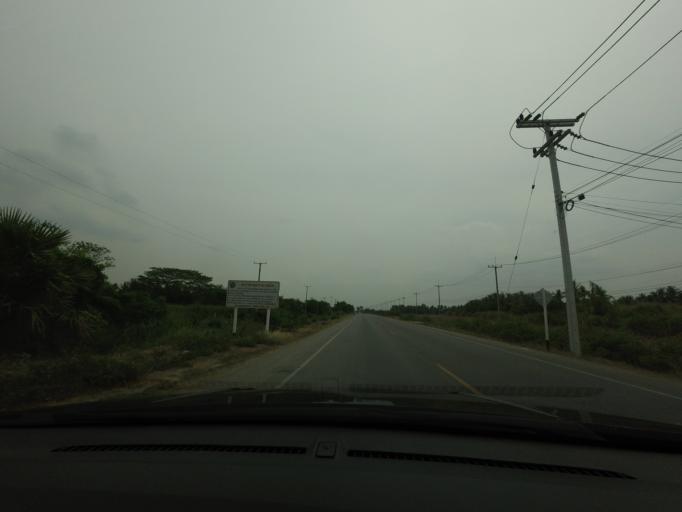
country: TH
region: Phetchaburi
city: Ban Laem
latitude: 13.1828
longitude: 99.9470
